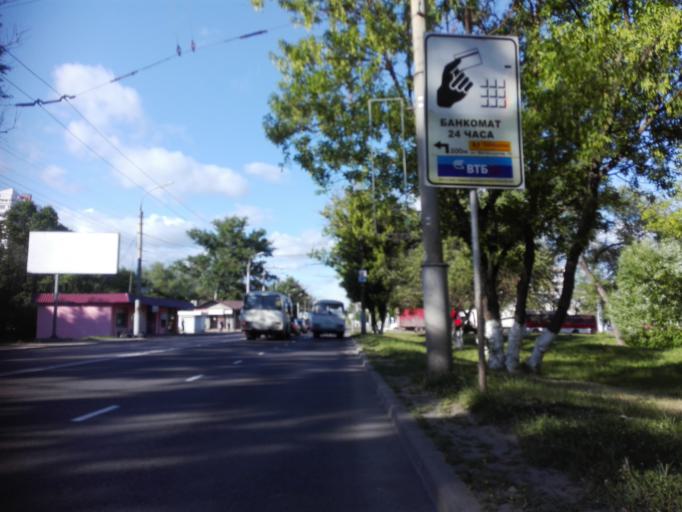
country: RU
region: Orjol
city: Orel
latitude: 53.0077
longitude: 36.1492
